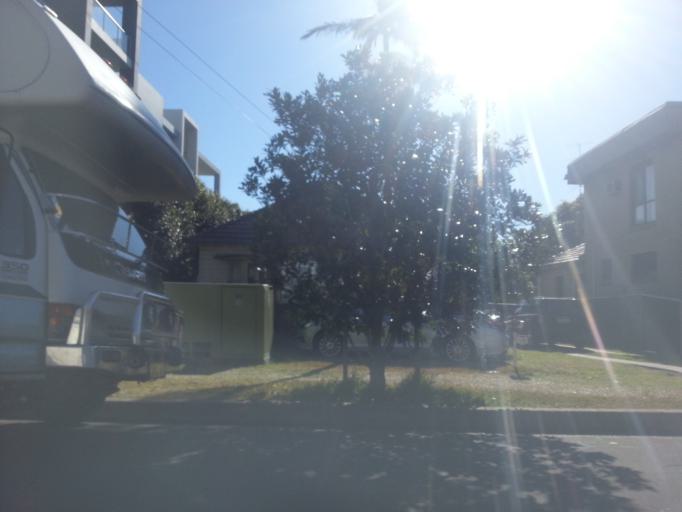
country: AU
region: New South Wales
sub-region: Wollongong
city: Gwynneville
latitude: -34.4129
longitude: 150.8967
